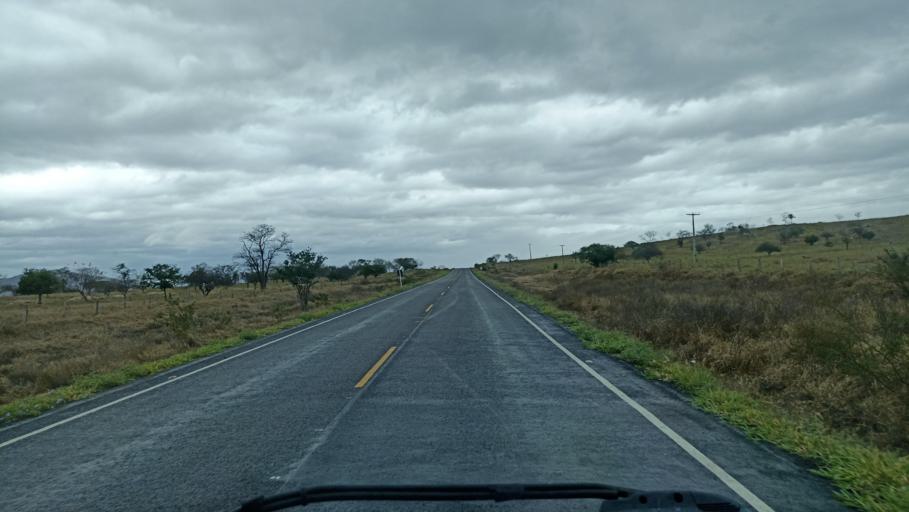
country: BR
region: Bahia
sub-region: Iacu
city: Iacu
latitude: -12.9655
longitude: -40.4887
